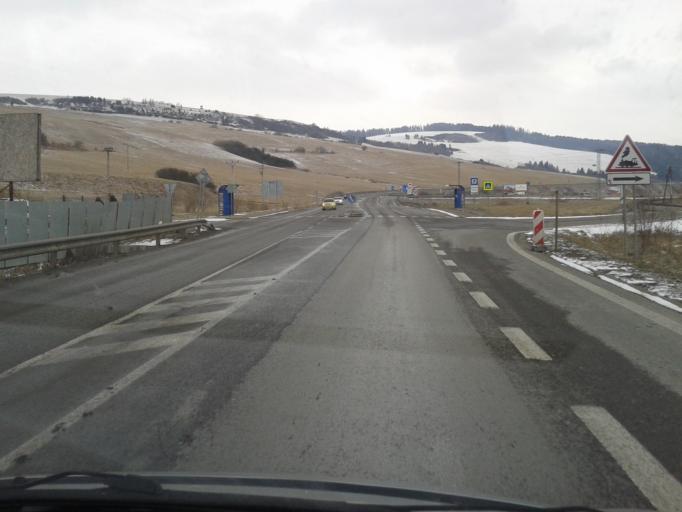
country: SK
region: Zilinsky
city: Tvrdosin
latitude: 49.3419
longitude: 19.5678
